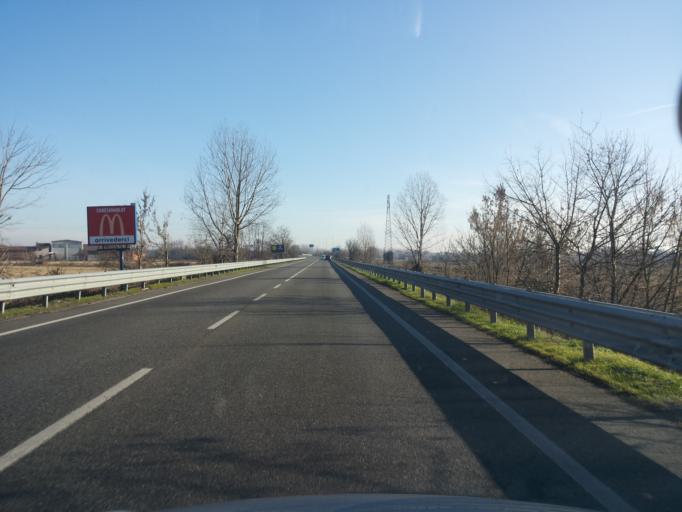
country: IT
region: Piedmont
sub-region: Provincia di Vercelli
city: Vercelli
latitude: 45.3411
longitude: 8.4222
